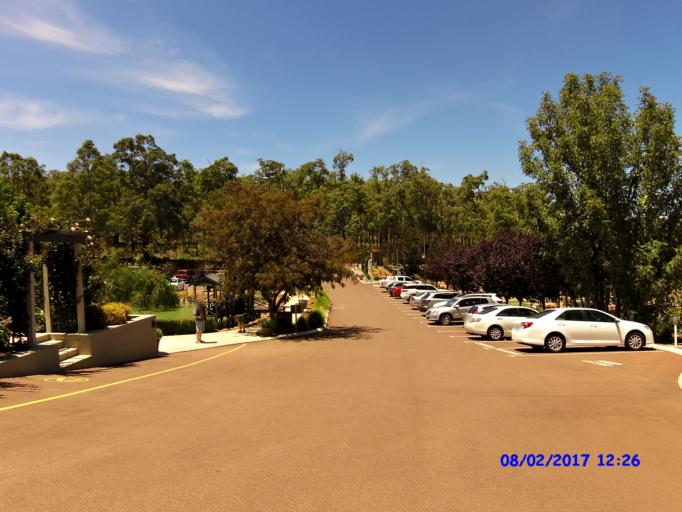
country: AU
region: Western Australia
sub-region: Kalamunda
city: Gooseberry Hill
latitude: -32.0250
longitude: 116.0729
